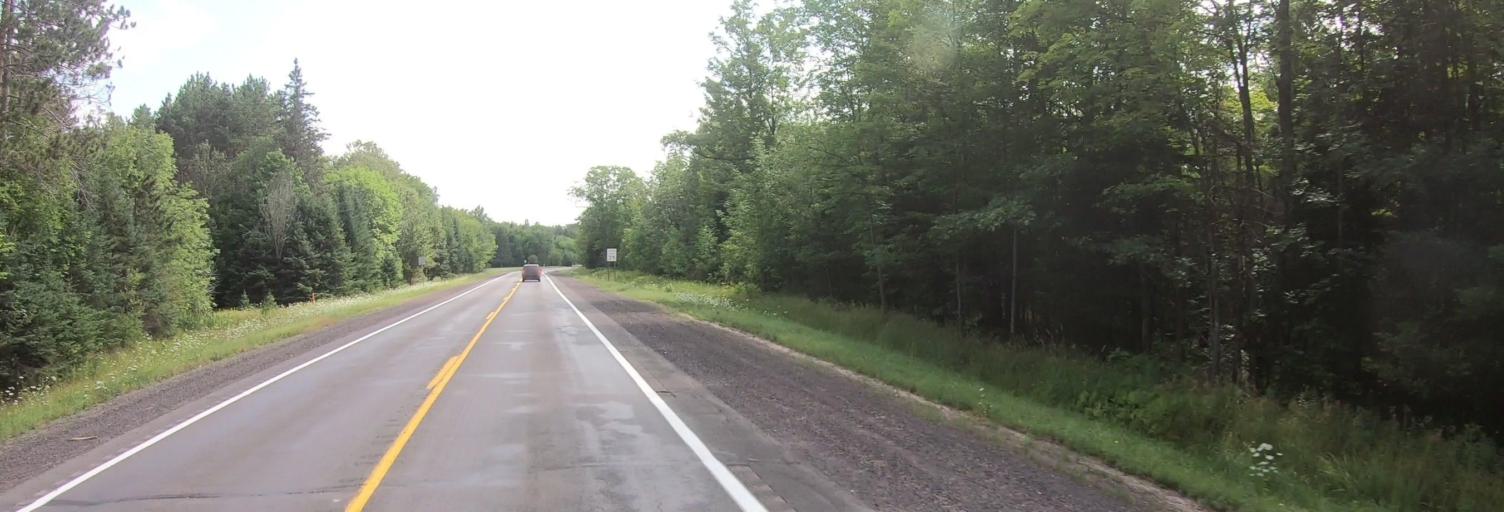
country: US
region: Michigan
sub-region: Ontonagon County
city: Ontonagon
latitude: 46.7667
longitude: -89.0751
